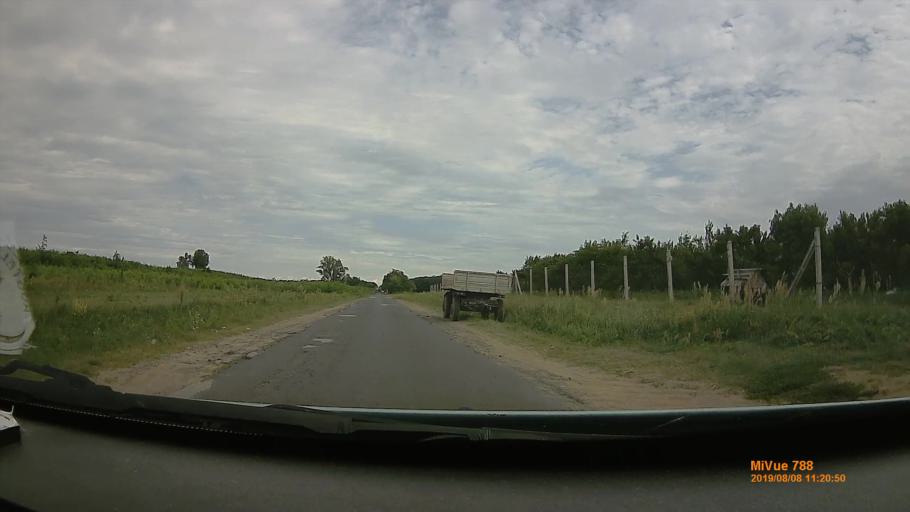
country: HU
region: Szabolcs-Szatmar-Bereg
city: Balkany
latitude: 47.7536
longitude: 21.8449
